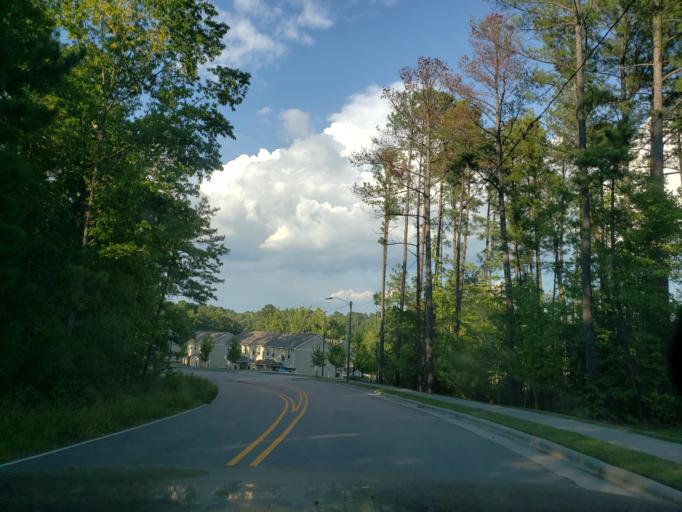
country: US
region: North Carolina
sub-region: Durham County
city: Durham
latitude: 35.9432
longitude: -78.9230
